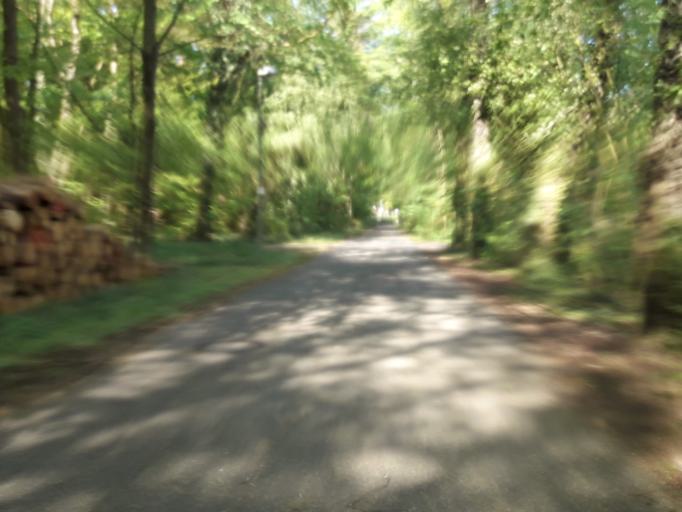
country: DE
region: North Rhine-Westphalia
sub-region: Regierungsbezirk Detmold
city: Paderborn
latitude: 51.7372
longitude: 8.7345
